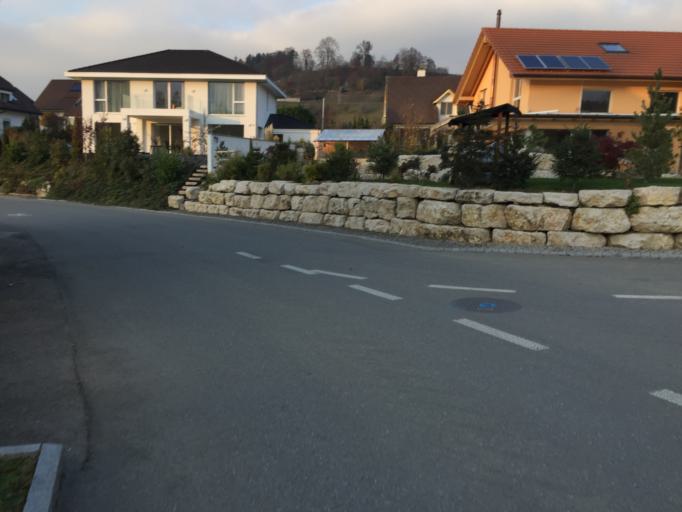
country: CH
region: Bern
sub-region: Bern-Mittelland District
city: Taegertschi
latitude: 46.8764
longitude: 7.5857
